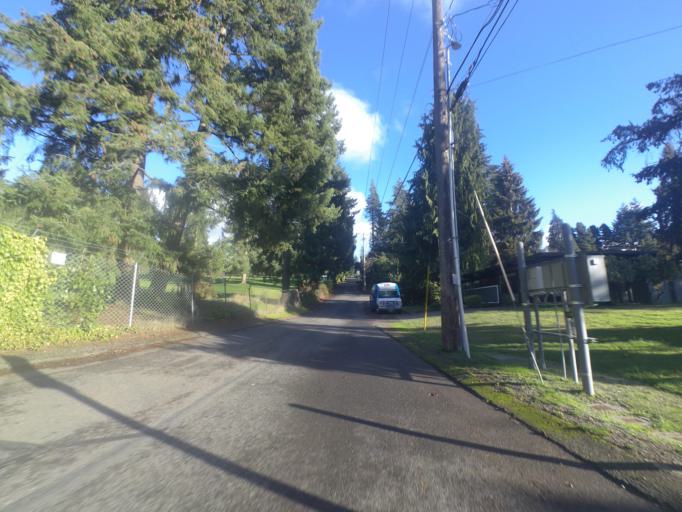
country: US
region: Washington
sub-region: Pierce County
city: Fircrest
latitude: 47.2282
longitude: -122.5258
